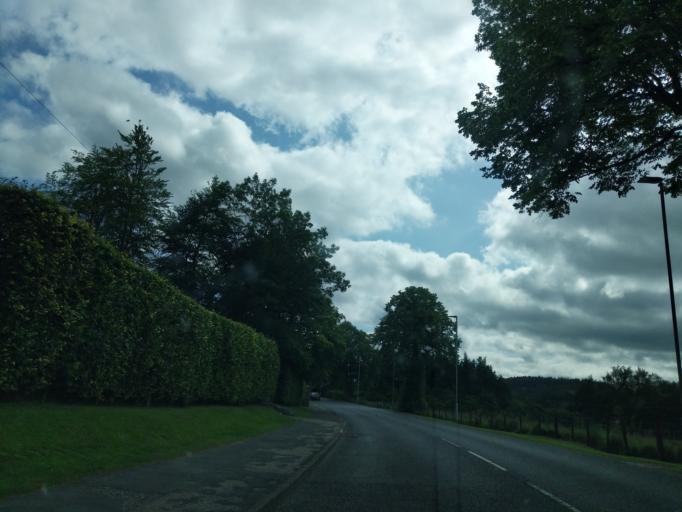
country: GB
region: Scotland
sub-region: Moray
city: Dufftown
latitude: 57.4510
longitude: -3.1310
